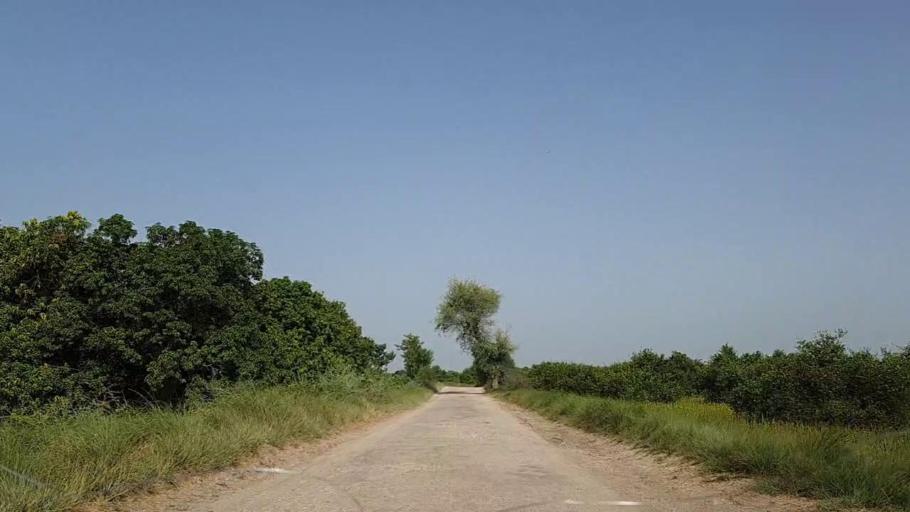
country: PK
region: Sindh
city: Kandiaro
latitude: 27.0670
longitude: 68.1765
